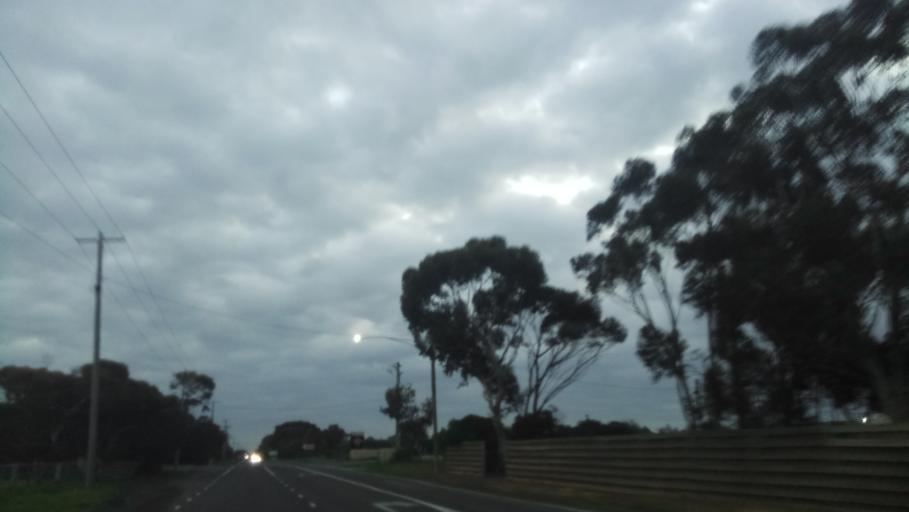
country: AU
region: Victoria
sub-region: Wyndham
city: Point Cook
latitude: -37.9168
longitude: 144.7506
